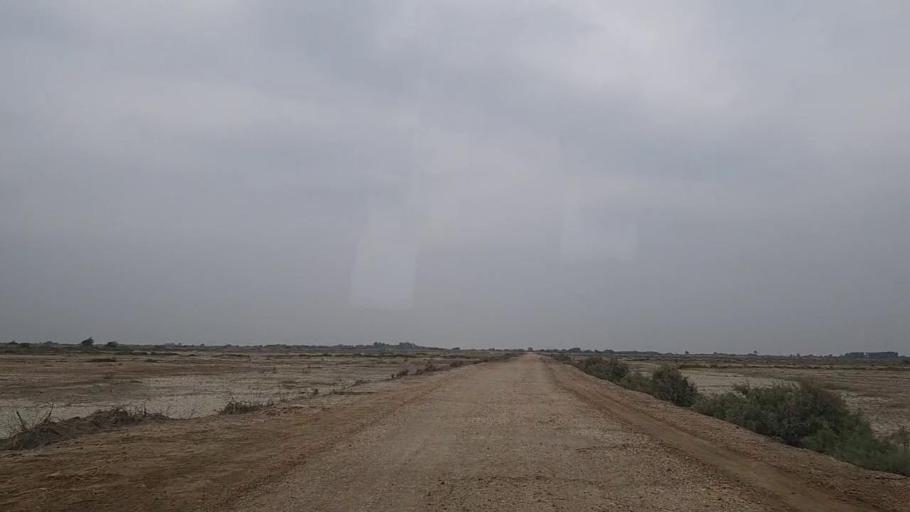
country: PK
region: Sindh
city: Mirpur Sakro
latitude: 24.6298
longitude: 67.7191
